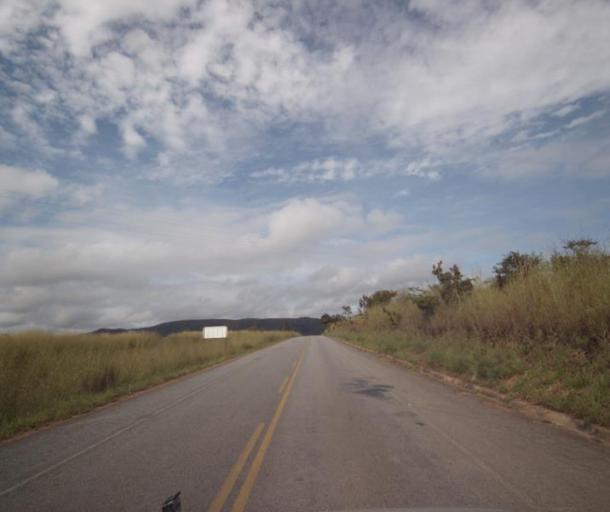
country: BR
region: Goias
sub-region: Pirenopolis
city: Pirenopolis
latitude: -15.6767
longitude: -48.7041
